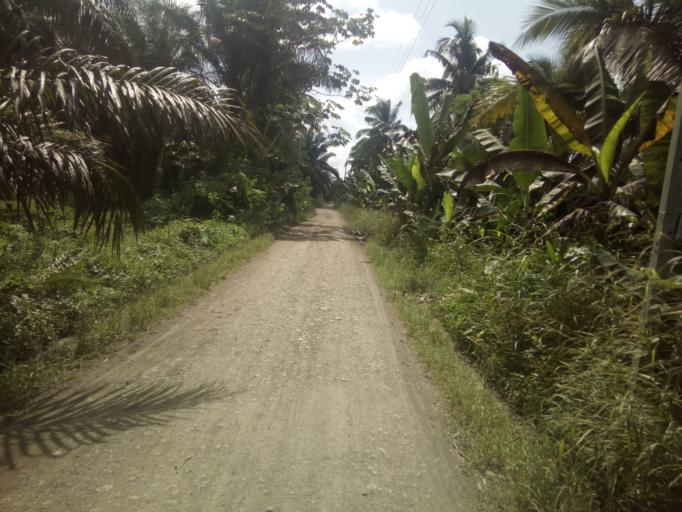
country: PH
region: Caraga
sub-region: Province of Agusan del Sur
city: Santa Josefa
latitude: 8.0337
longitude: 126.0120
